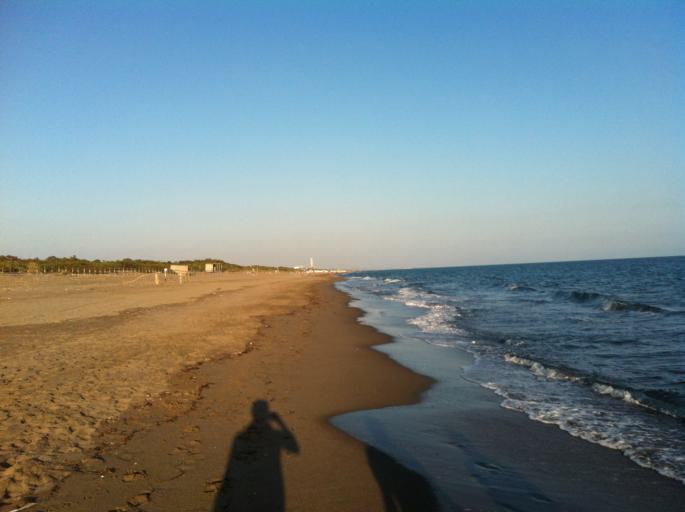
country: IT
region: Latium
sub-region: Provincia di Viterbo
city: Pescia Romana
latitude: 42.3814
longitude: 11.4370
